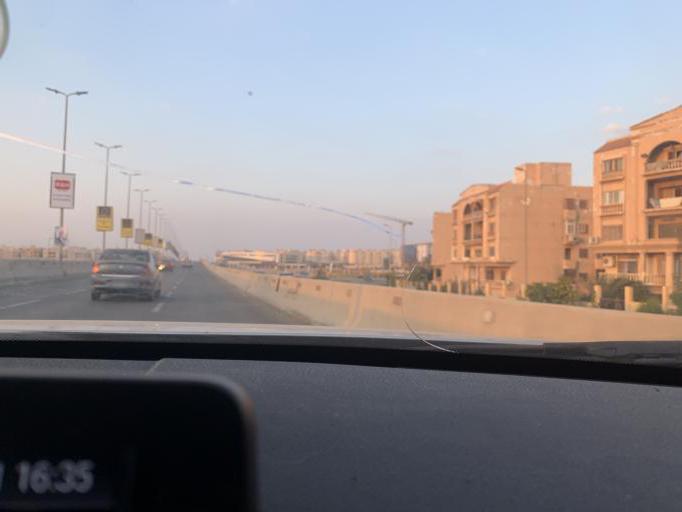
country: EG
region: Muhafazat al Qalyubiyah
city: Al Khankah
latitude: 30.0235
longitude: 31.4749
